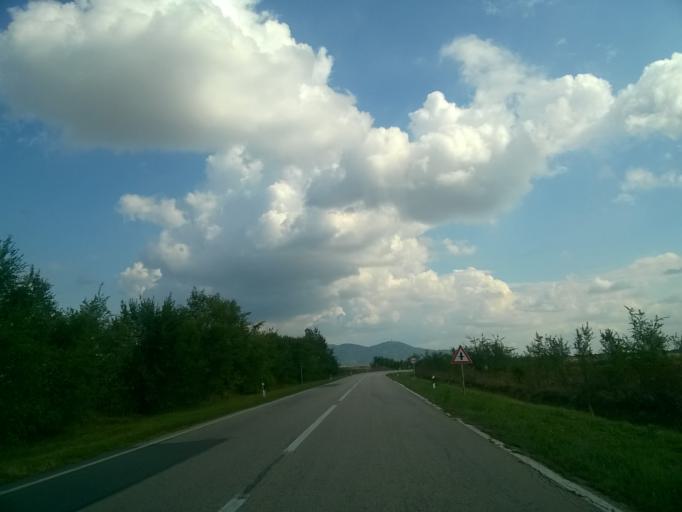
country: RS
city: Pavlis
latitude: 45.1548
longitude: 21.2526
